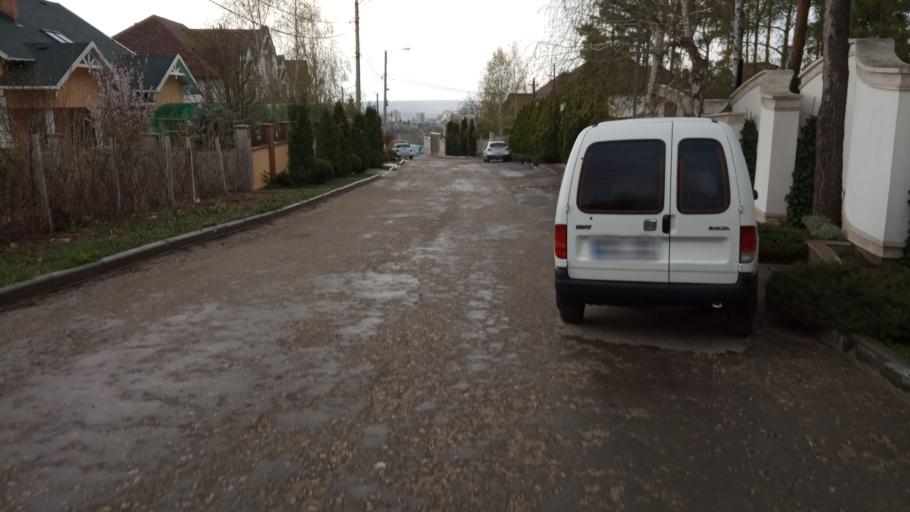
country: MD
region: Chisinau
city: Chisinau
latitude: 47.0096
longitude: 28.8102
